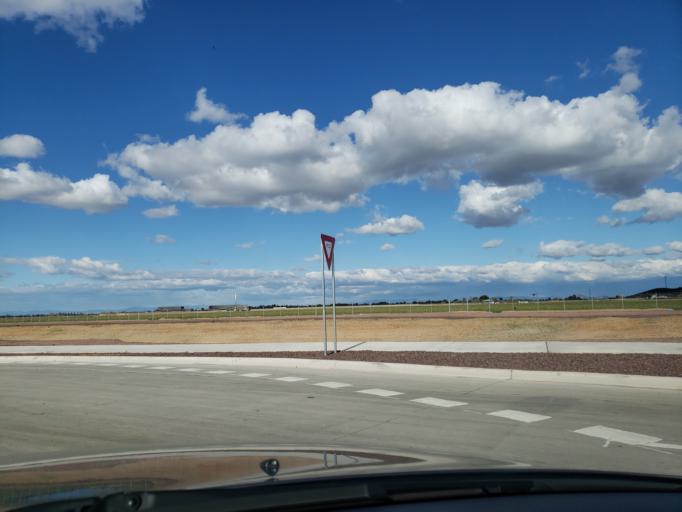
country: US
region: Arizona
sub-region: Maricopa County
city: Laveen
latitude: 33.3344
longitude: -112.1755
